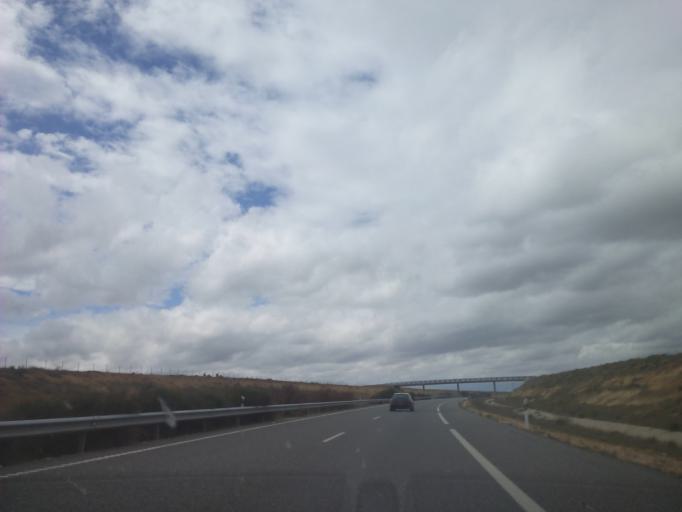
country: ES
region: Castille and Leon
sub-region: Provincia de Salamanca
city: Machacon
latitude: 40.9202
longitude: -5.5283
